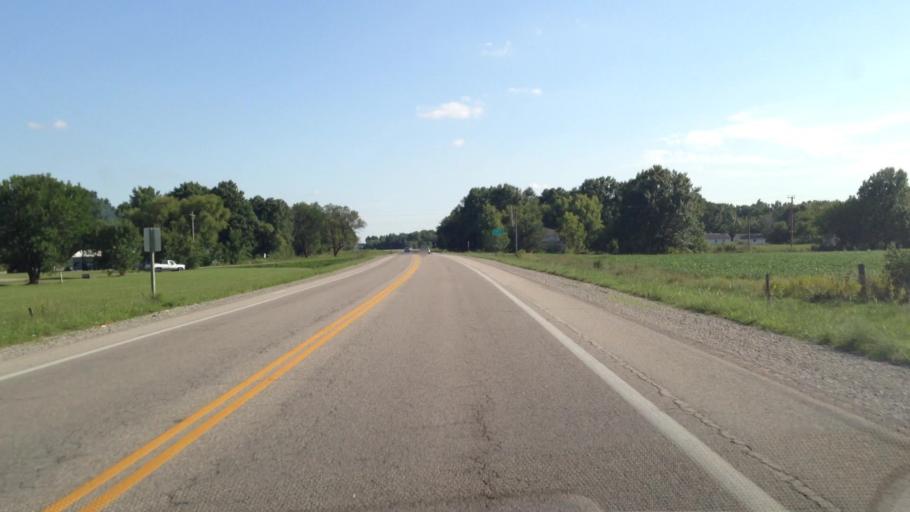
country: US
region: Kansas
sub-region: Crawford County
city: Arma
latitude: 37.5302
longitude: -94.7111
